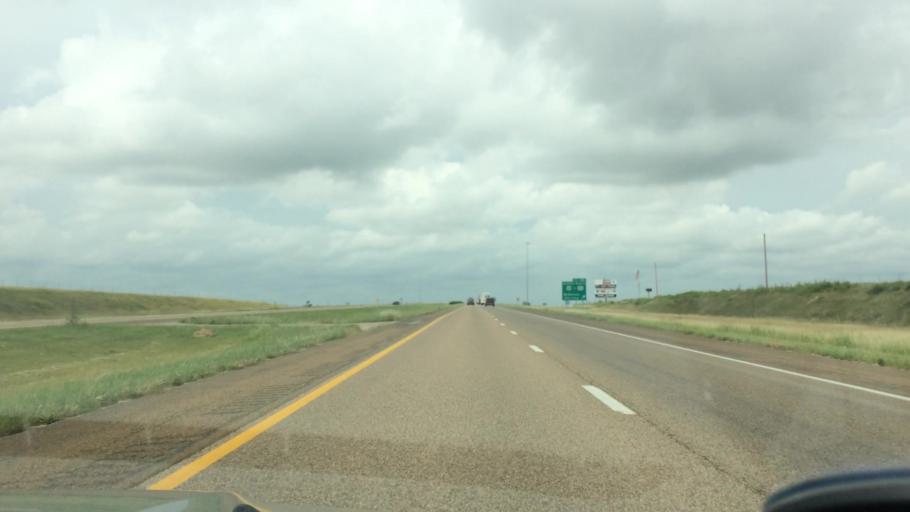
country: US
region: Kansas
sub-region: Trego County
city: WaKeeney
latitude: 39.0096
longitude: -99.8646
